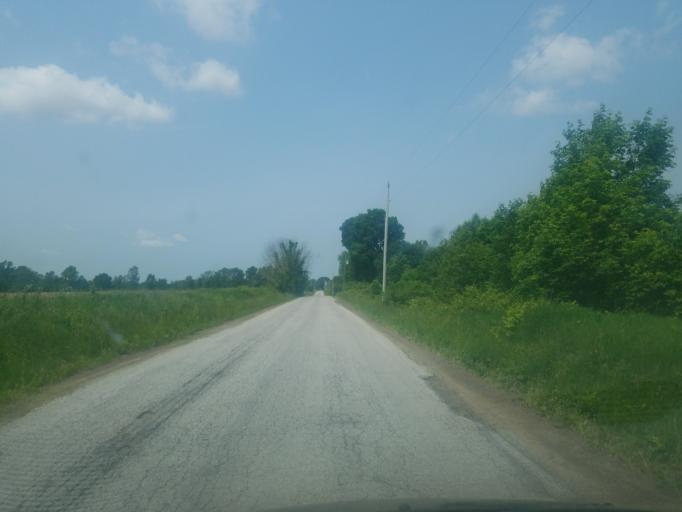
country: US
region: Ohio
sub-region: Morrow County
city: Mount Gilead
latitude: 40.6399
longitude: -82.8275
